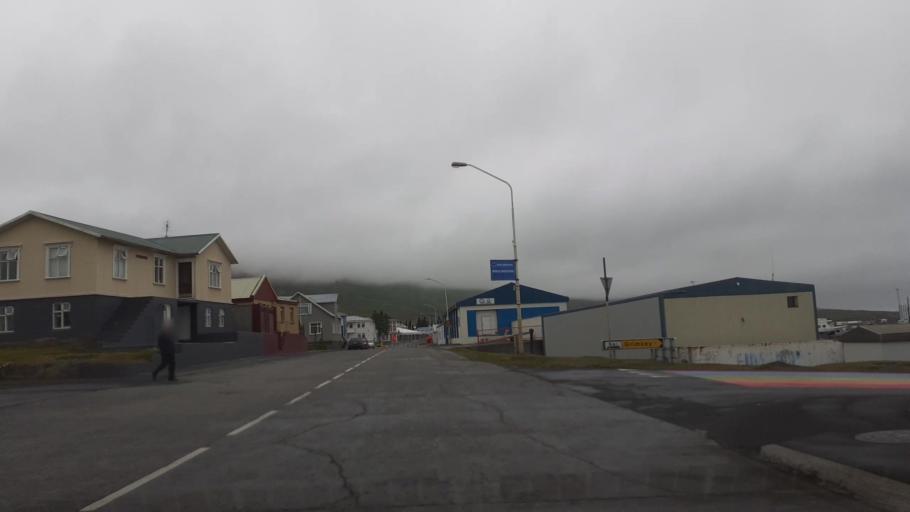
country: IS
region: Northeast
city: Dalvik
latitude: 65.9703
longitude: -18.5281
